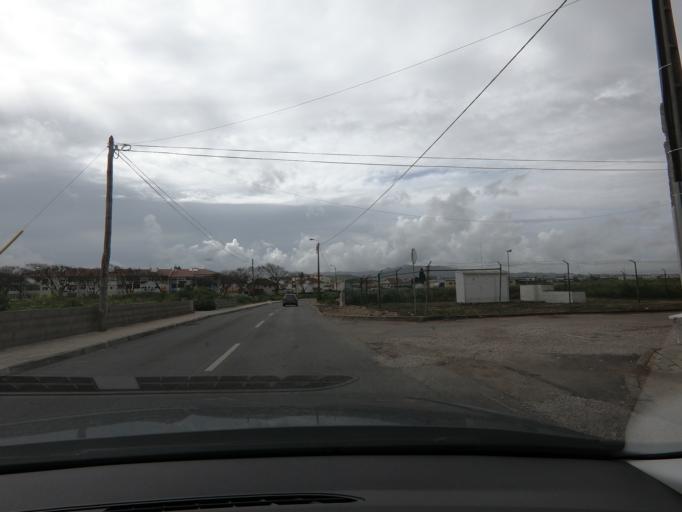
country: PT
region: Lisbon
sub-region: Cascais
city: Sao Domingos de Rana
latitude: 38.7356
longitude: -9.3347
